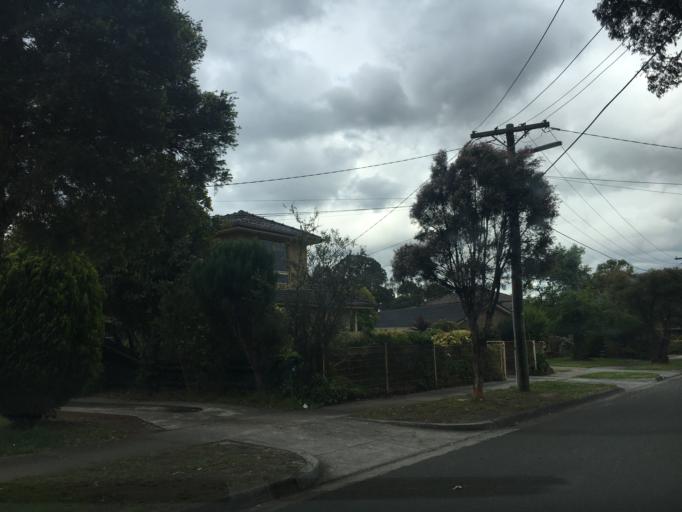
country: AU
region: Victoria
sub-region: Whitehorse
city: Vermont South
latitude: -37.8725
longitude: 145.1781
